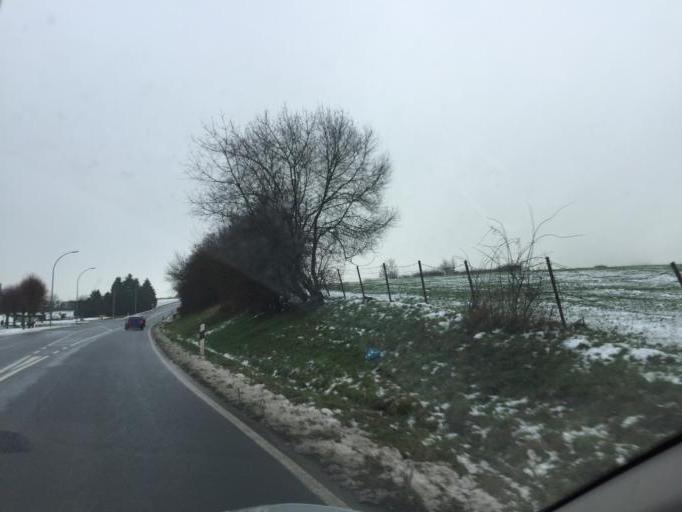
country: LU
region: Diekirch
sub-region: Canton de Diekirch
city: Niederfeulen
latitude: 49.8518
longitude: 6.0388
